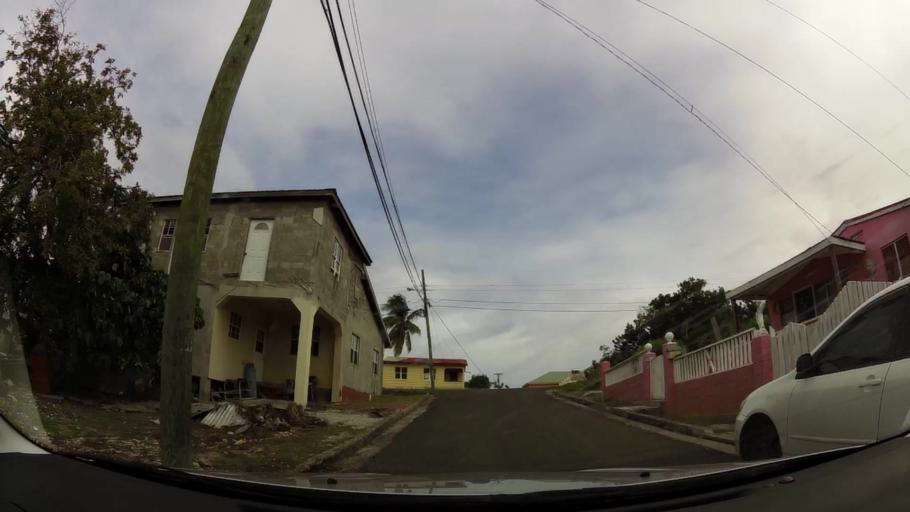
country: AG
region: Saint Peter
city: Parham
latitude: 17.0866
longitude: -61.7101
